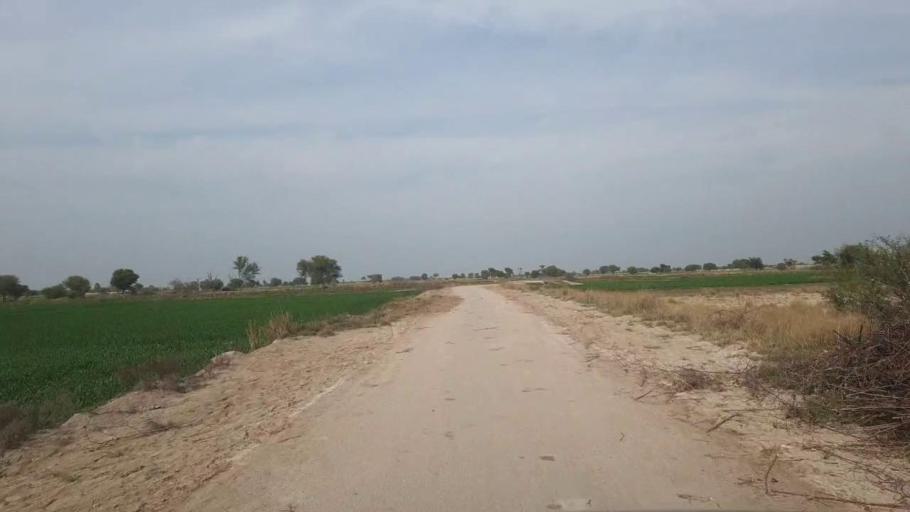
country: PK
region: Sindh
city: Shahpur Chakar
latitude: 26.1122
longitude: 68.5049
